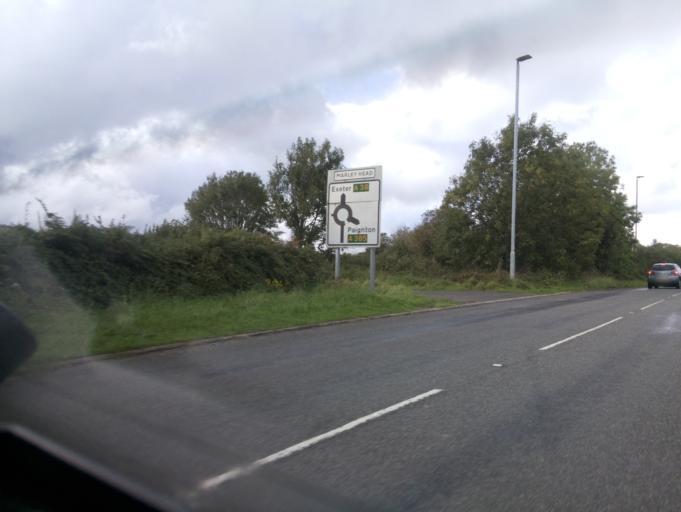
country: GB
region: England
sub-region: Devon
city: South Brent
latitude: 50.4326
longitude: -3.8038
